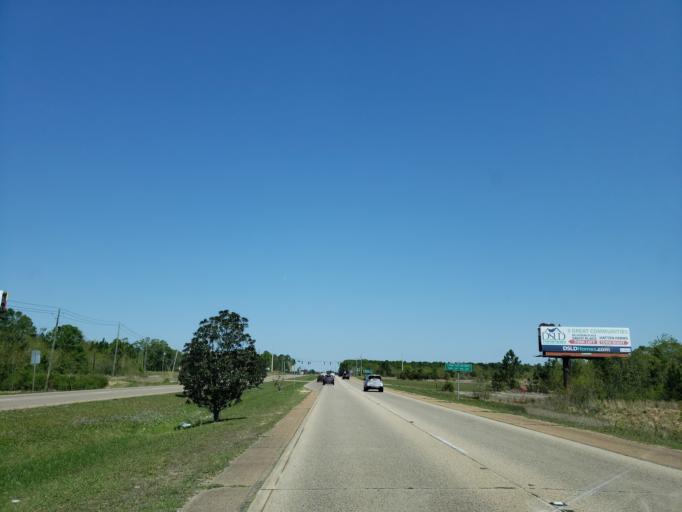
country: US
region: Mississippi
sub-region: Harrison County
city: Lyman
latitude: 30.4983
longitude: -89.1059
